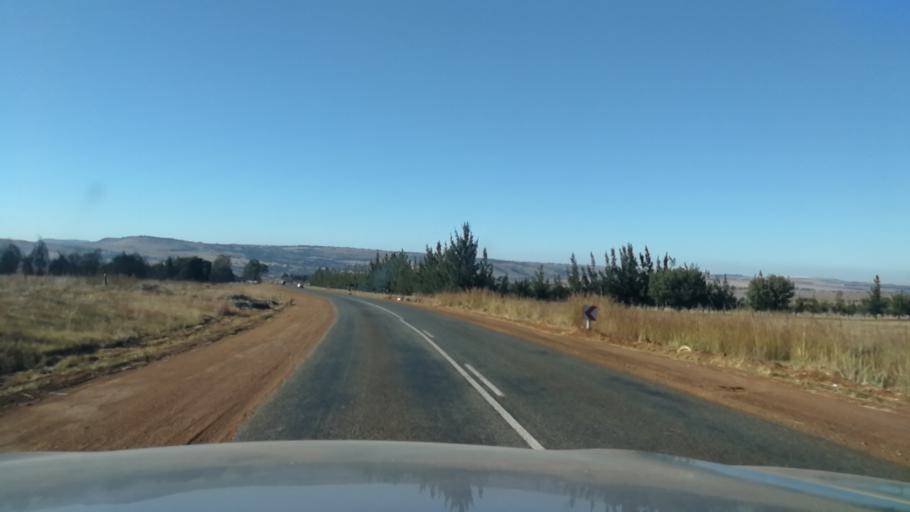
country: ZA
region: Gauteng
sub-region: West Rand District Municipality
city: Krugersdorp
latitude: -26.0009
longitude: 27.7023
